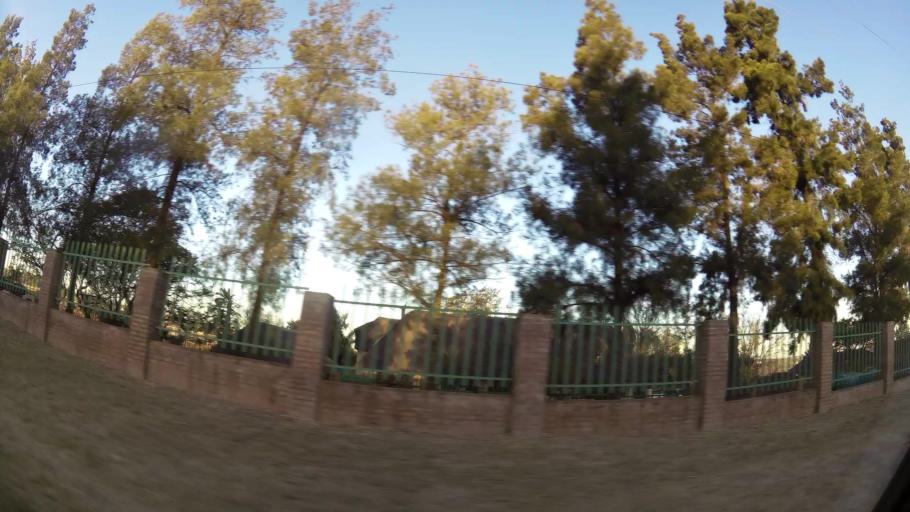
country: ZA
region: Gauteng
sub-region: City of Johannesburg Metropolitan Municipality
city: Diepsloot
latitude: -25.9424
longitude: 28.0537
